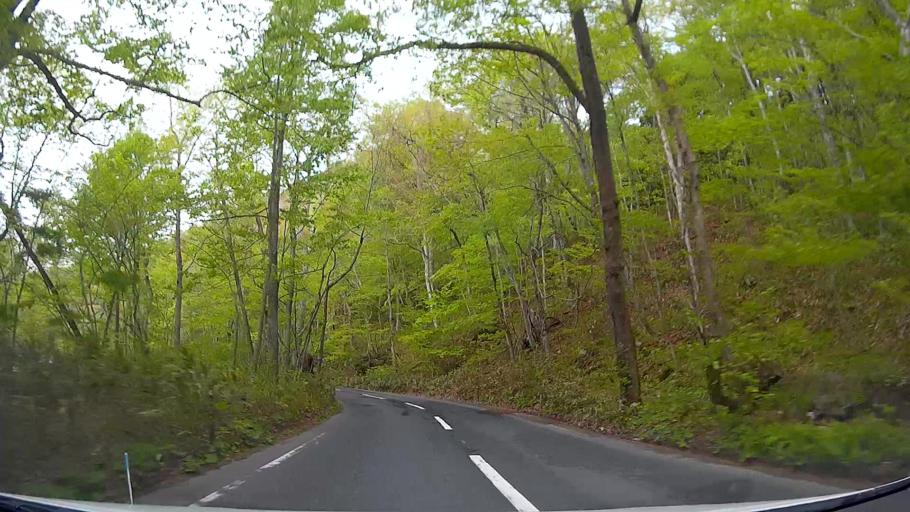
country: JP
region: Aomori
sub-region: Aomori Shi
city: Furudate
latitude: 40.5695
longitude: 140.9790
